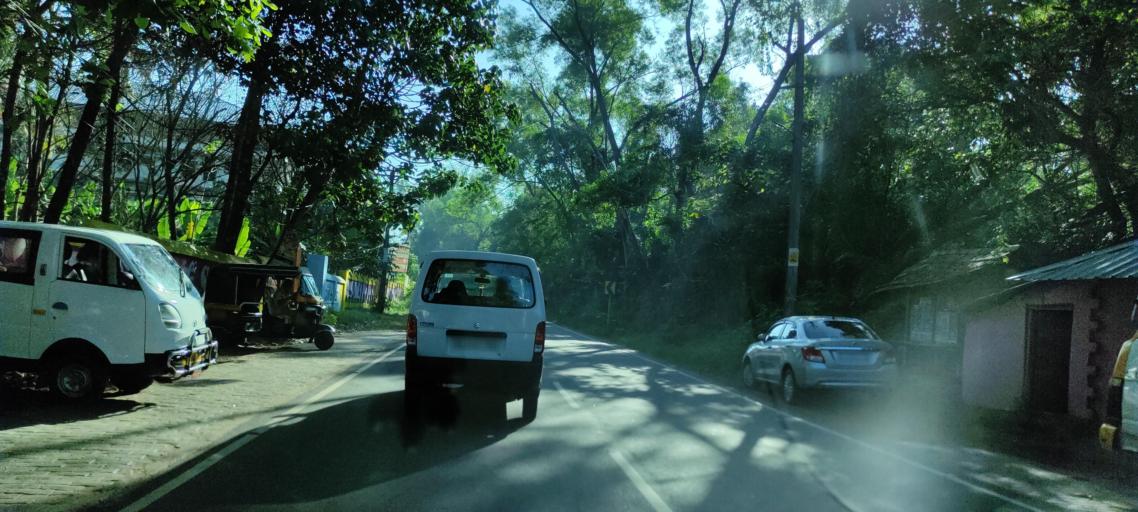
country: IN
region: Kerala
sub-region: Alappuzha
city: Kattanam
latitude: 9.1751
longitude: 76.6235
